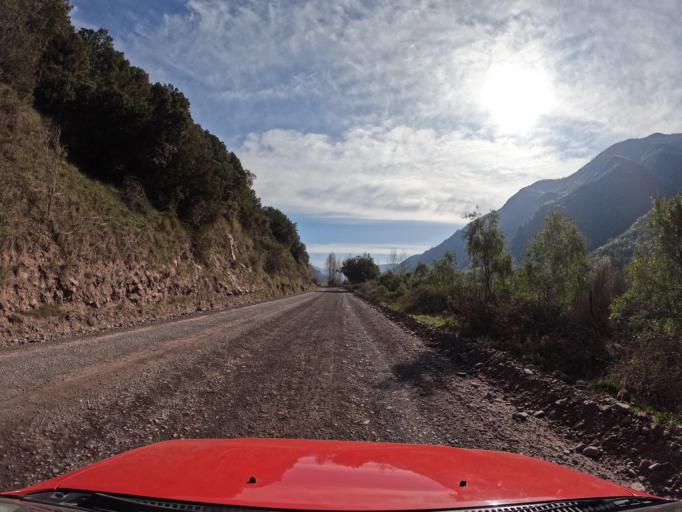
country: CL
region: O'Higgins
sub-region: Provincia de Colchagua
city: Chimbarongo
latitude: -34.9999
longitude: -70.7838
